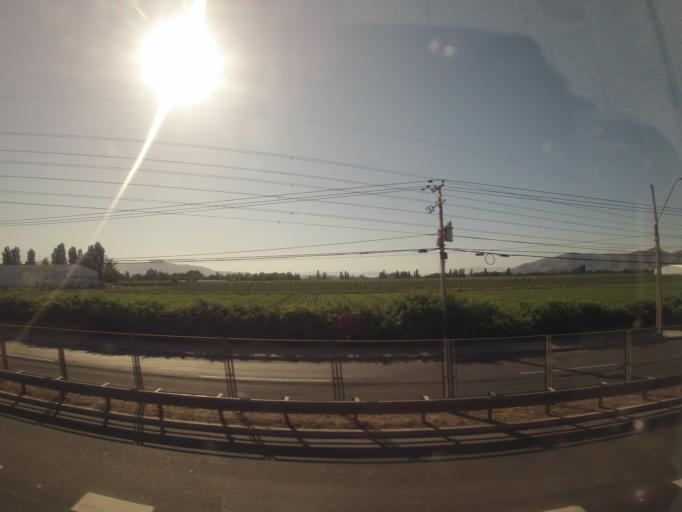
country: CL
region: Santiago Metropolitan
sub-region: Provincia de Maipo
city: San Bernardo
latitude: -33.6511
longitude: -70.7133
